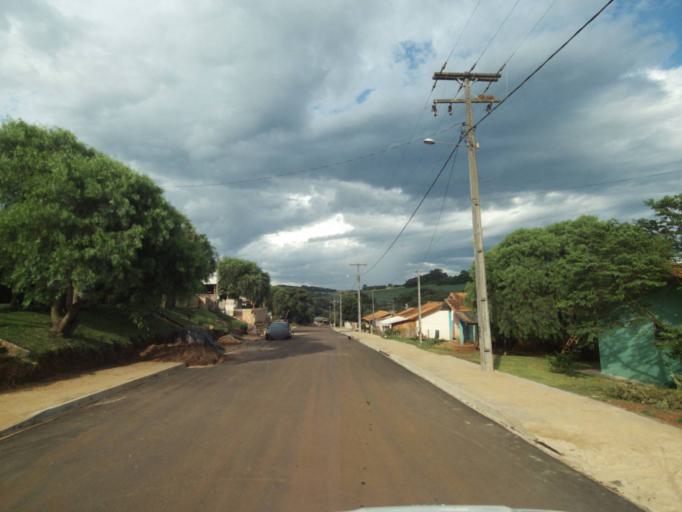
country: BR
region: Parana
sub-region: Laranjeiras Do Sul
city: Laranjeiras do Sul
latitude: -25.4947
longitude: -52.5245
